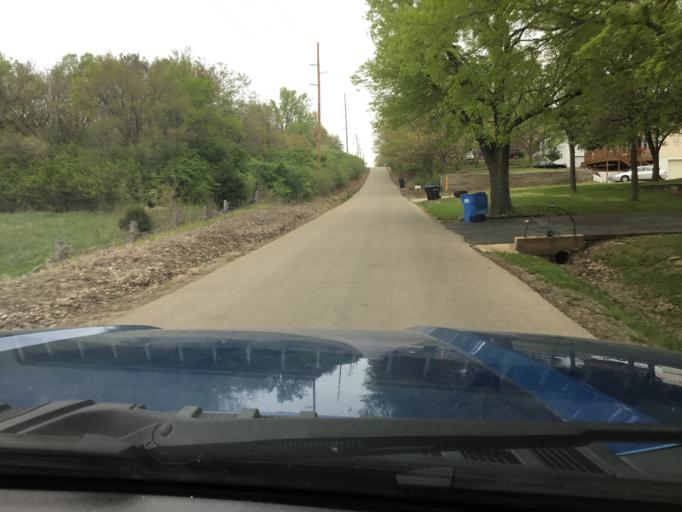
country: US
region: Kansas
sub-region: Shawnee County
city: Topeka
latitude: 39.1033
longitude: -95.6874
